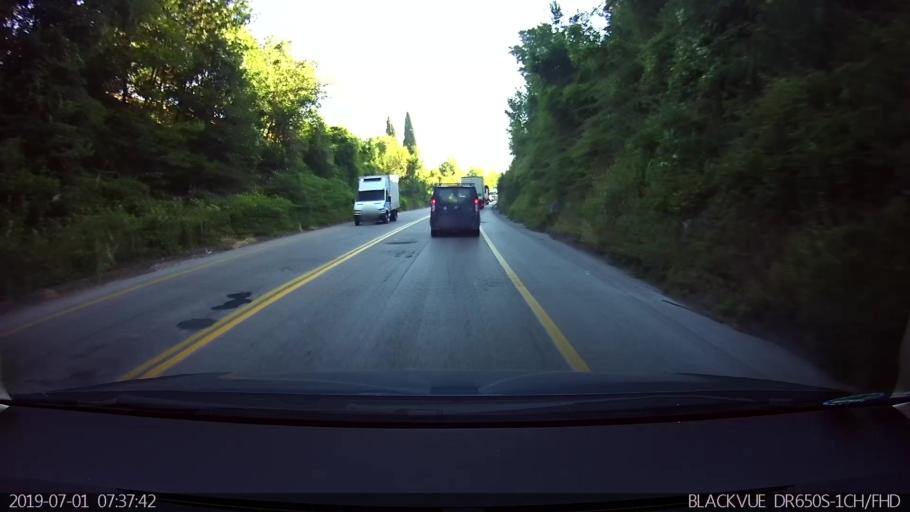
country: IT
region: Latium
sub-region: Provincia di Frosinone
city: Giuliano di Roma
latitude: 41.5397
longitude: 13.2672
